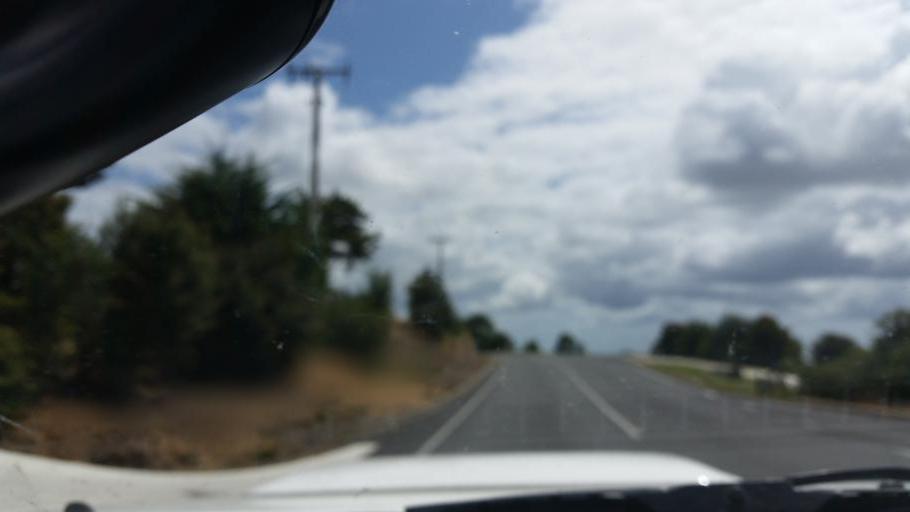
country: NZ
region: Auckland
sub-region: Auckland
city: Wellsford
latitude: -36.1398
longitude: 174.5570
